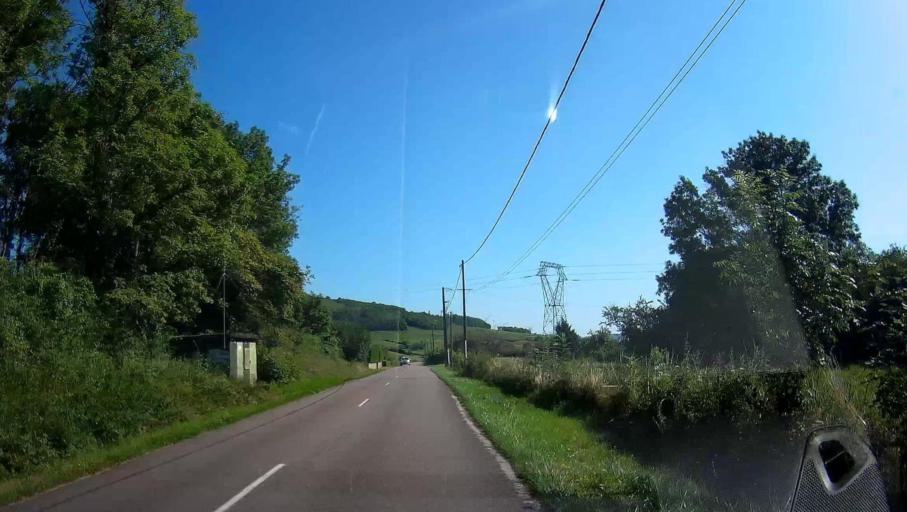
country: FR
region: Bourgogne
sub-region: Departement de la Cote-d'Or
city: Nolay
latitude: 46.9169
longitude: 4.6035
